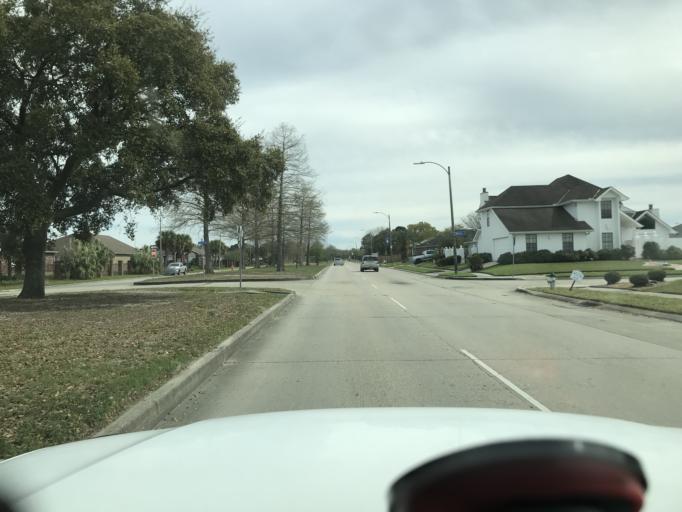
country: US
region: Louisiana
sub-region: Saint Bernard Parish
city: Chalmette
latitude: 30.0347
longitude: -89.9517
